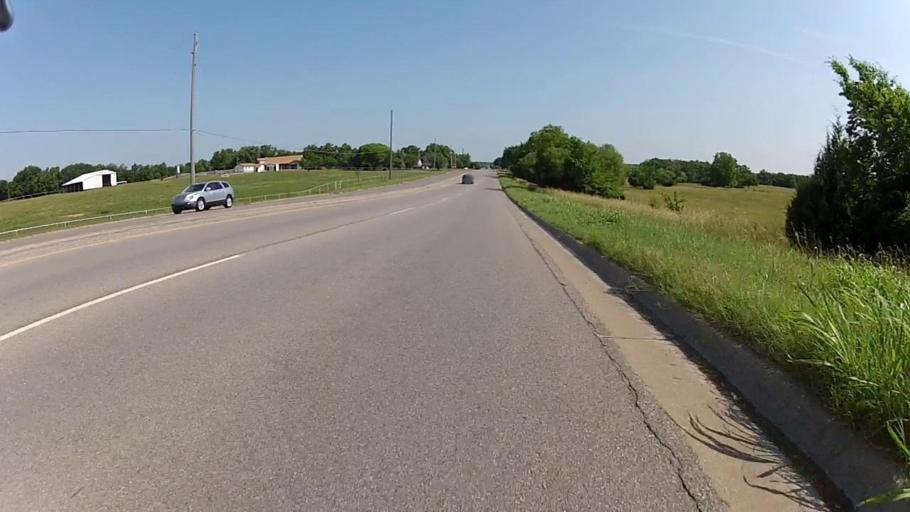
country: US
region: Kansas
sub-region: Montgomery County
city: Independence
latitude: 37.2010
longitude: -95.7106
